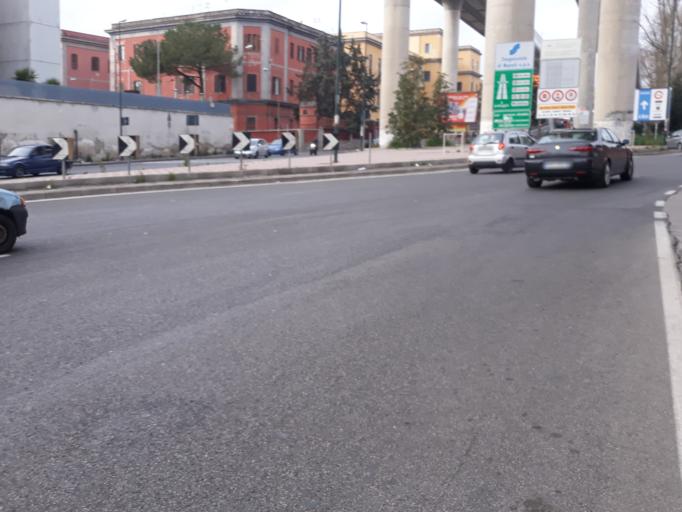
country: IT
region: Campania
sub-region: Provincia di Napoli
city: Napoli
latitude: 40.8627
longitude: 14.2761
